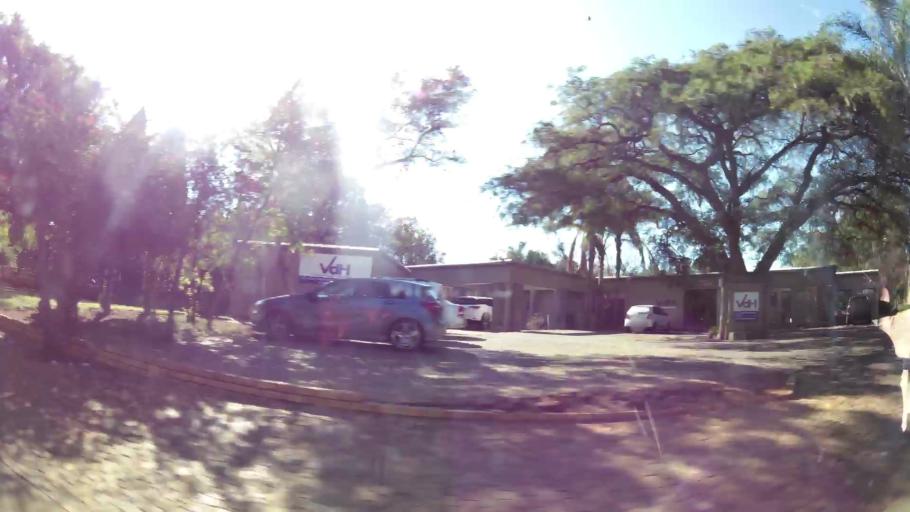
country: ZA
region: Gauteng
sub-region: City of Tshwane Metropolitan Municipality
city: Pretoria
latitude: -25.6780
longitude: 28.2167
